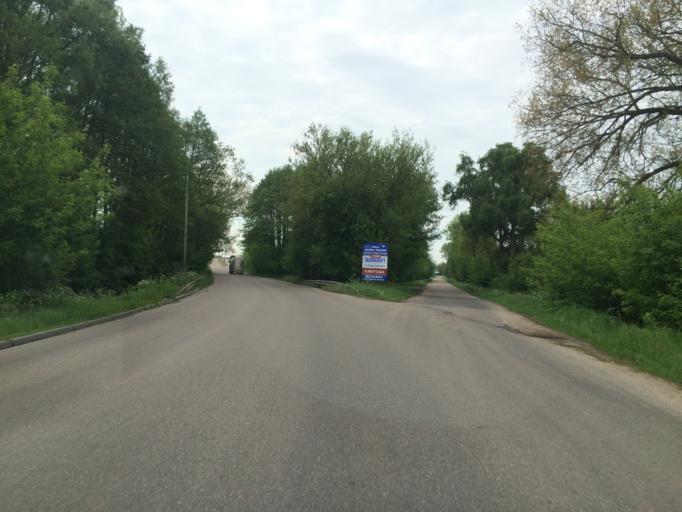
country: PL
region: Masovian Voivodeship
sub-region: Powiat mlawski
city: Mlawa
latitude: 53.0987
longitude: 20.3732
